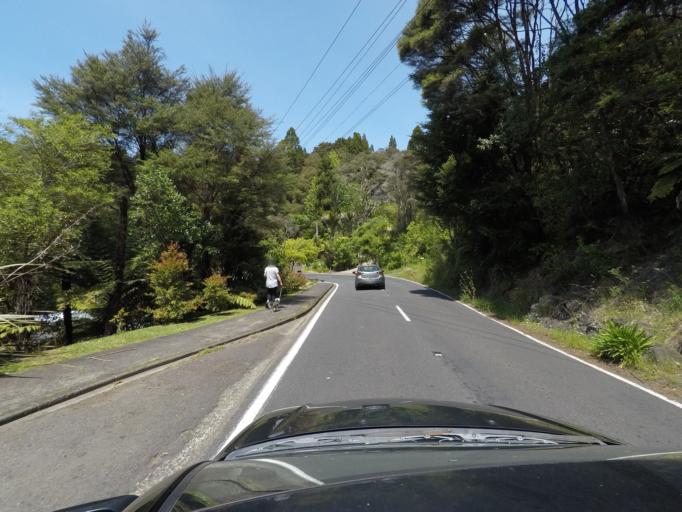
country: NZ
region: Auckland
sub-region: Auckland
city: Titirangi
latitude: -36.9579
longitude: 174.6386
